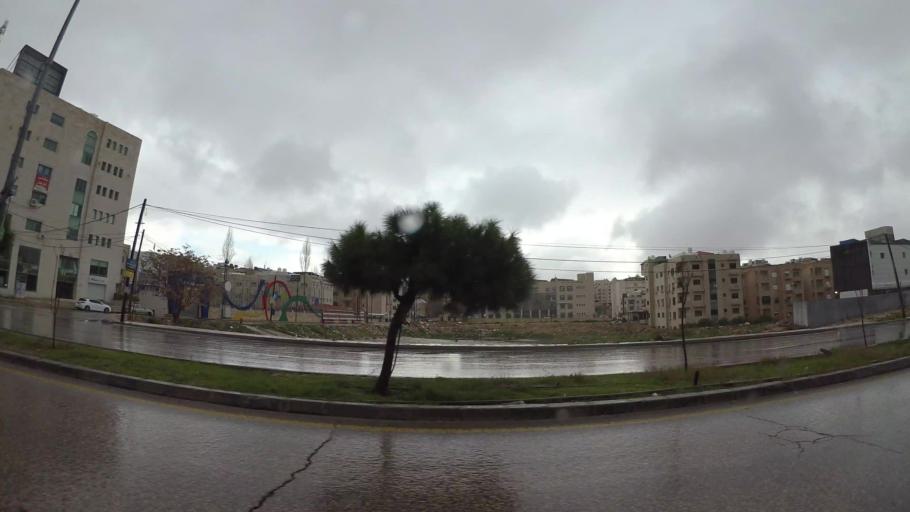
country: JO
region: Amman
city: Al Jubayhah
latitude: 31.9869
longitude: 35.8665
